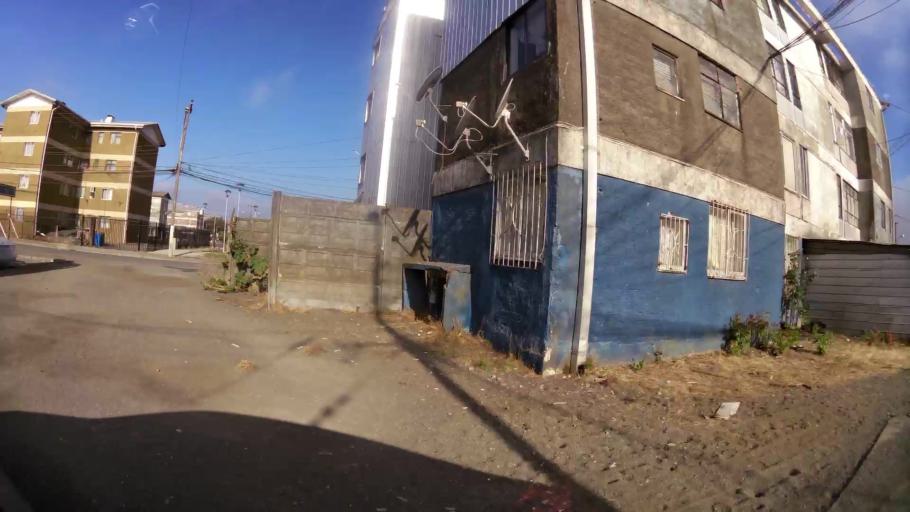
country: CL
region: Biobio
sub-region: Provincia de Concepcion
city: Concepcion
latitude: -36.7902
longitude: -73.0919
